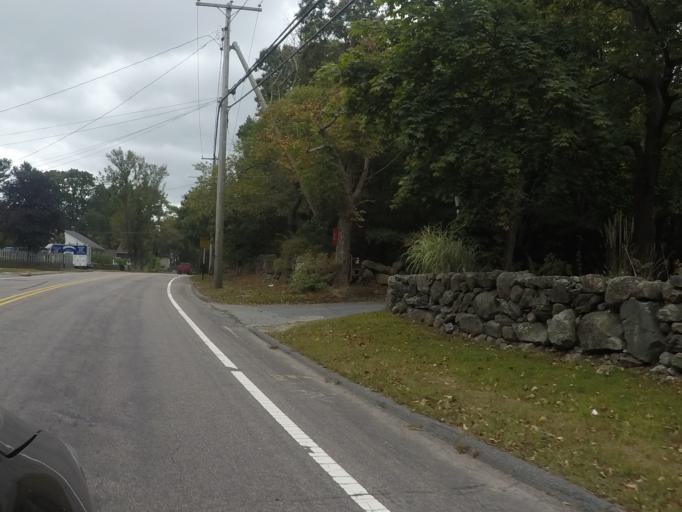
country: US
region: Massachusetts
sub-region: Bristol County
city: Smith Mills
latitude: 41.6375
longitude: -70.9869
